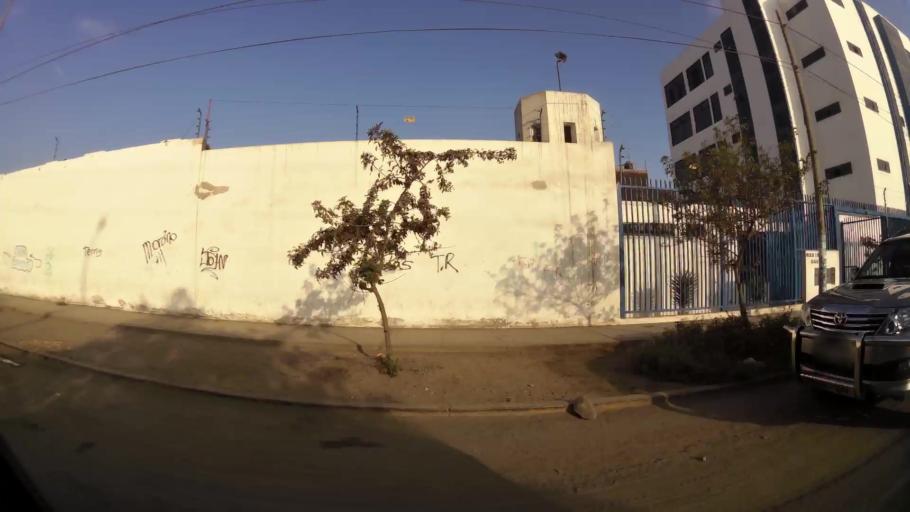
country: PE
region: La Libertad
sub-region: Provincia de Trujillo
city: El Porvenir
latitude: -8.0963
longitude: -79.0055
